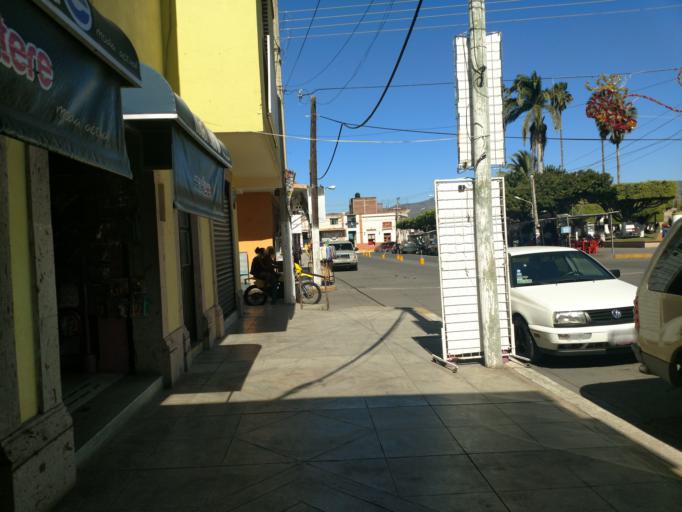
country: MX
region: Nayarit
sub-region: Ahuacatlan
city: Ahuacatlan
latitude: 21.0512
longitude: -104.4845
